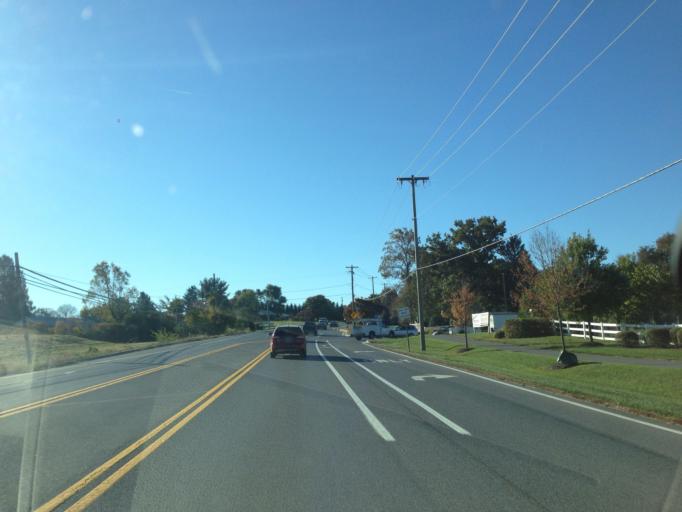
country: US
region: Maryland
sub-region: Montgomery County
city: Clarksburg
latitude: 39.2322
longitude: -77.2373
